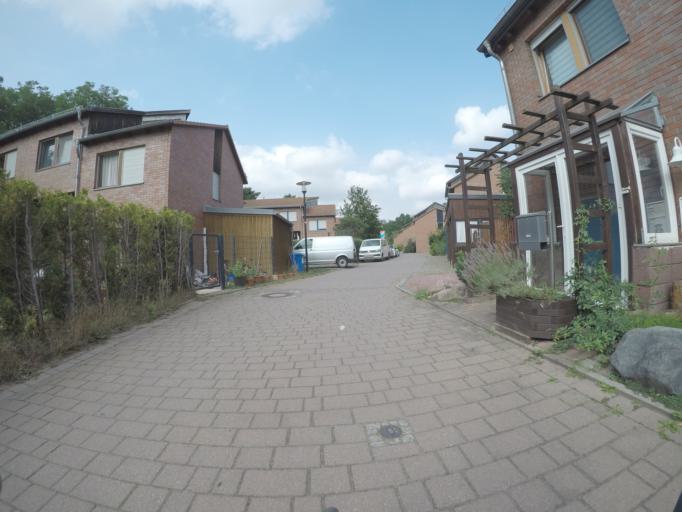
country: DE
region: Berlin
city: Lichtenrade
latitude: 52.3465
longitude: 13.4235
